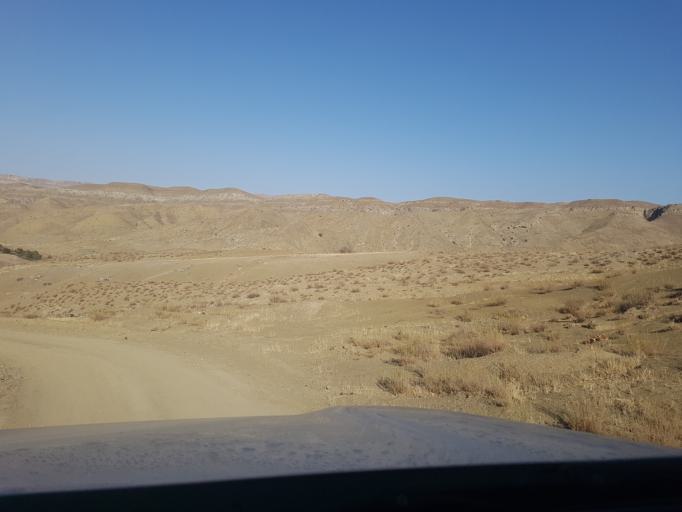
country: TM
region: Balkan
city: Magtymguly
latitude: 38.3020
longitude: 56.7778
